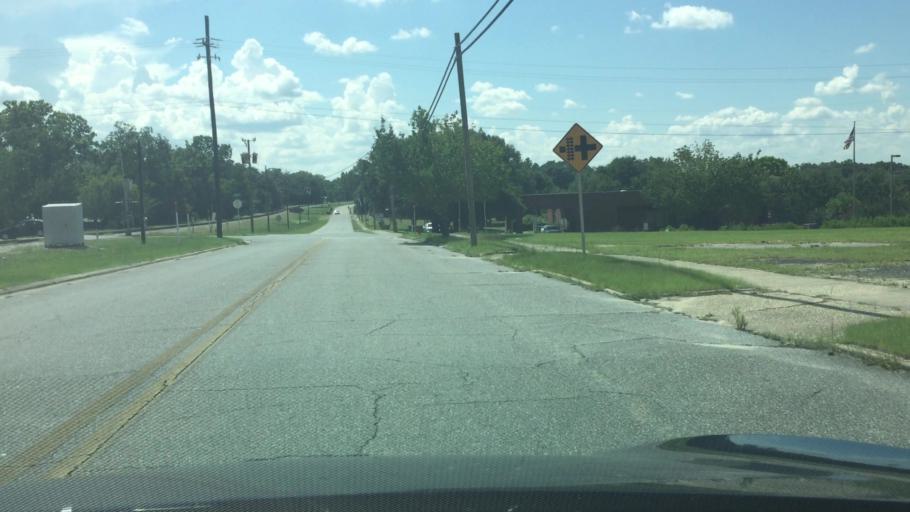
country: US
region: Florida
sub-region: Walton County
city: DeFuniak Springs
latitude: 30.7205
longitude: -86.1171
